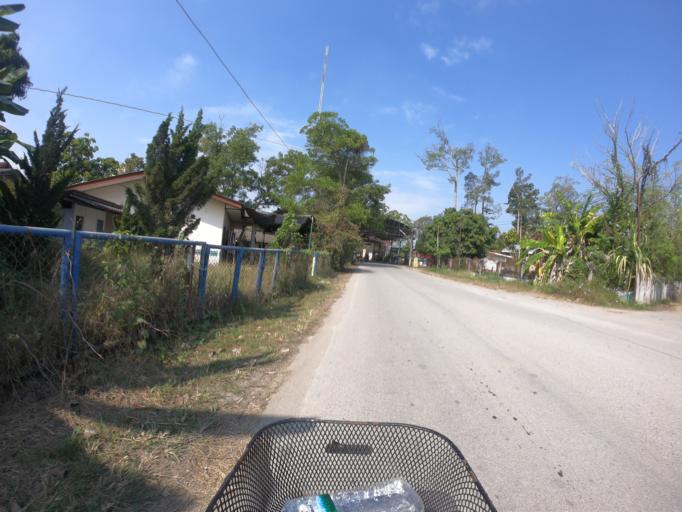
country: TH
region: Chiang Mai
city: Saraphi
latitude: 18.7110
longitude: 99.0616
